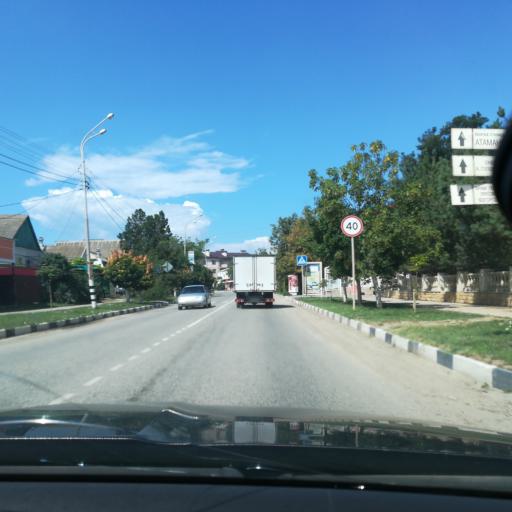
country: RU
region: Krasnodarskiy
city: Taman'
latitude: 45.2174
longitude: 36.7252
